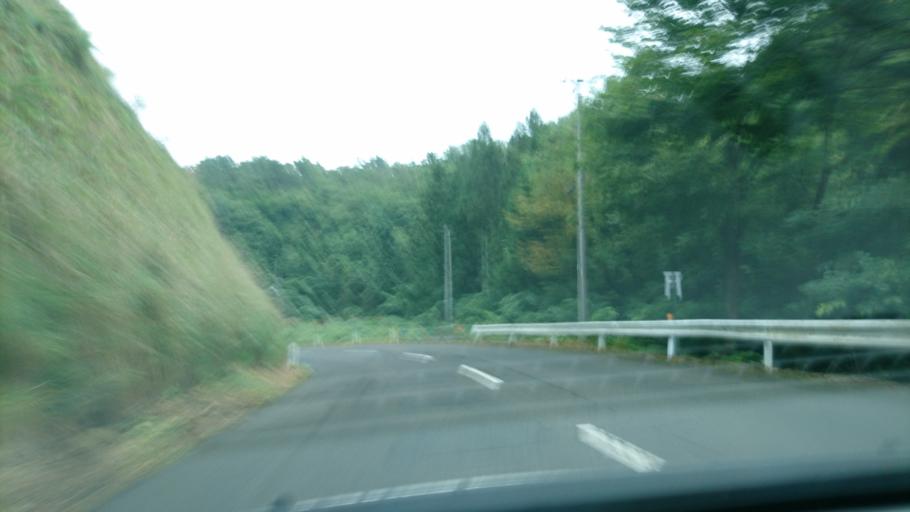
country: JP
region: Iwate
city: Ichinoseki
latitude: 38.8932
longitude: 141.0111
